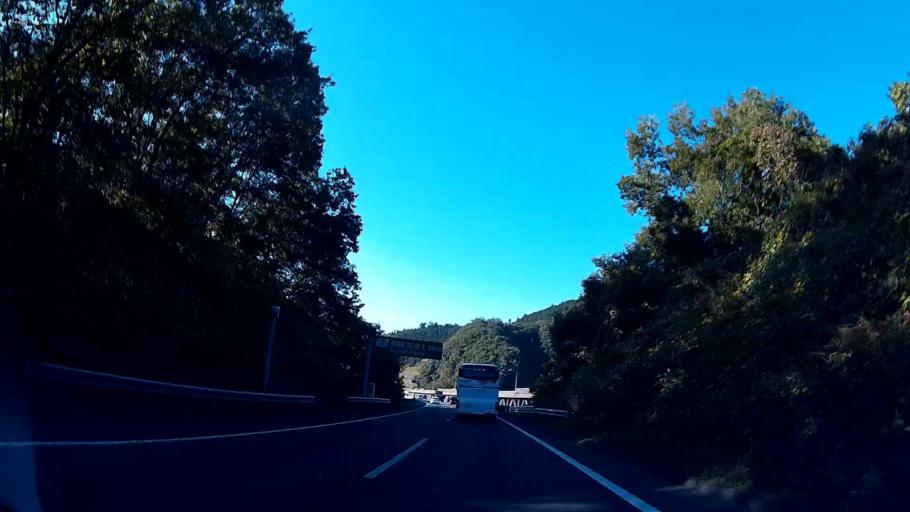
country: JP
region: Yamanashi
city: Uenohara
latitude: 35.6327
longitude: 139.2054
